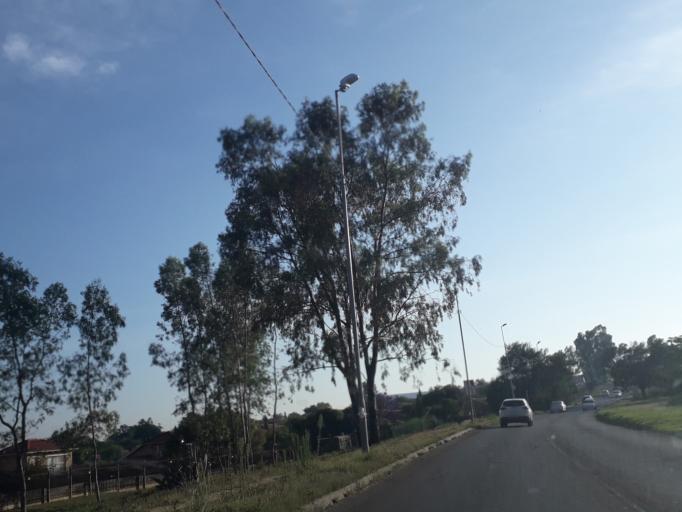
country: ZA
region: Gauteng
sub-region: City of Johannesburg Metropolitan Municipality
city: Roodepoort
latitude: -26.1018
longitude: 27.9012
